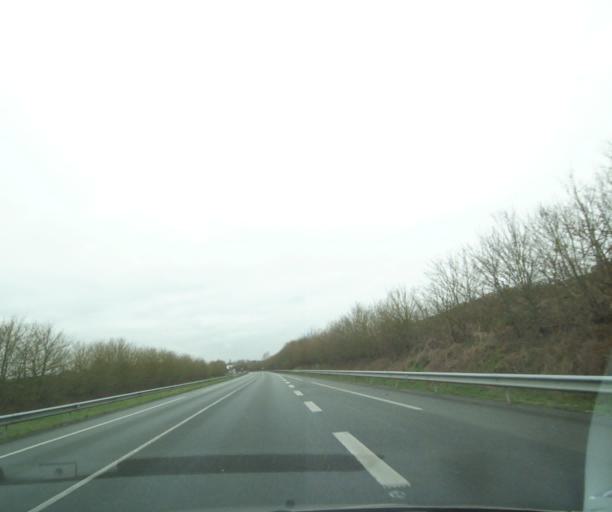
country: FR
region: Picardie
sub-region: Departement de l'Oise
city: Noyon
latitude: 49.5721
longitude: 3.0287
